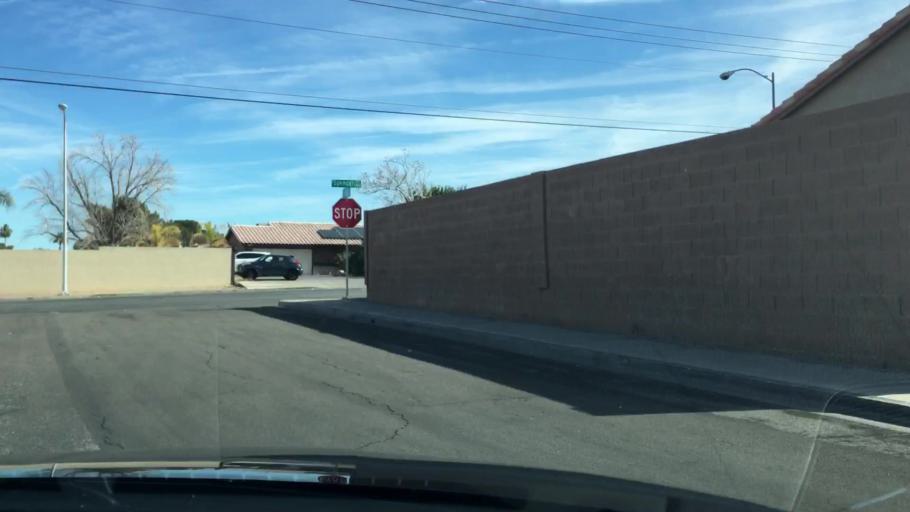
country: US
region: Nevada
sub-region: Clark County
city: Whitney
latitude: 36.0474
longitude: -115.1277
